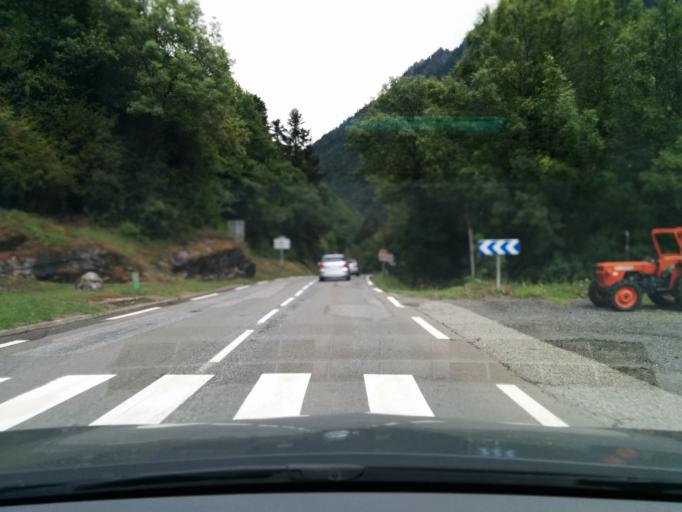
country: FR
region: Midi-Pyrenees
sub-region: Departement des Hautes-Pyrenees
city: Saint-Lary-Soulan
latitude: 42.7869
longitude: 0.2481
